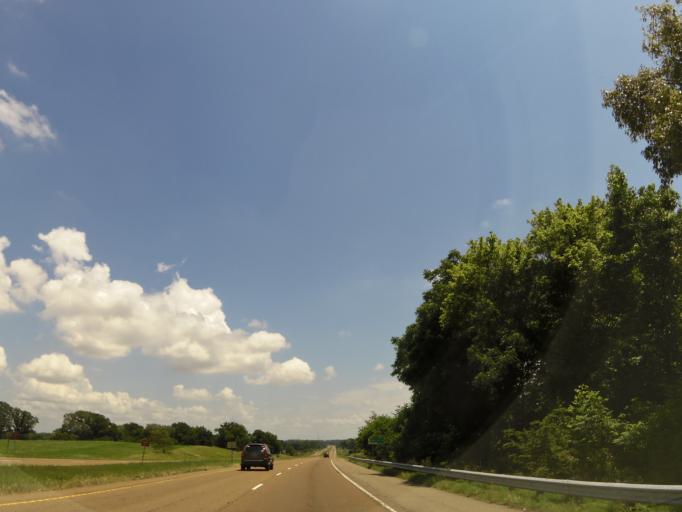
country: US
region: Tennessee
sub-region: Lauderdale County
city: Halls
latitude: 35.9379
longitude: -89.2947
